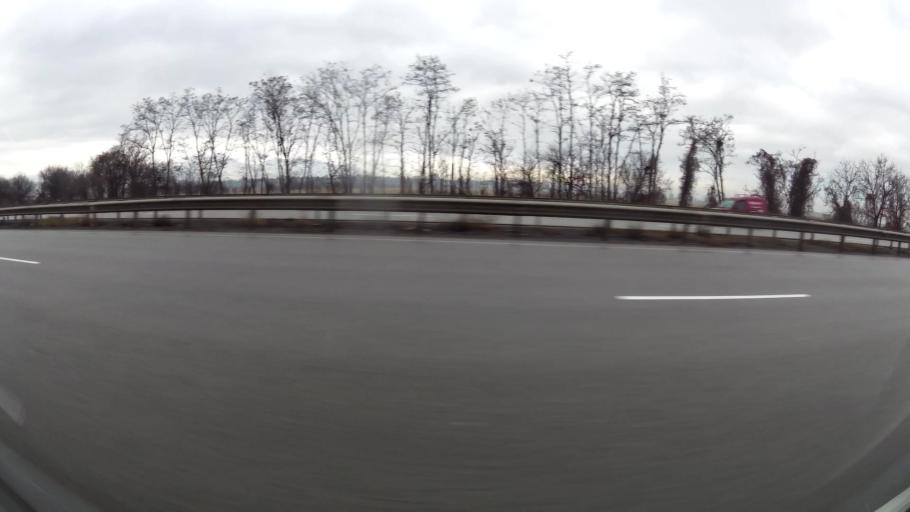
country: BG
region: Sofia-Capital
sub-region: Stolichna Obshtina
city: Sofia
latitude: 42.6408
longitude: 23.4506
